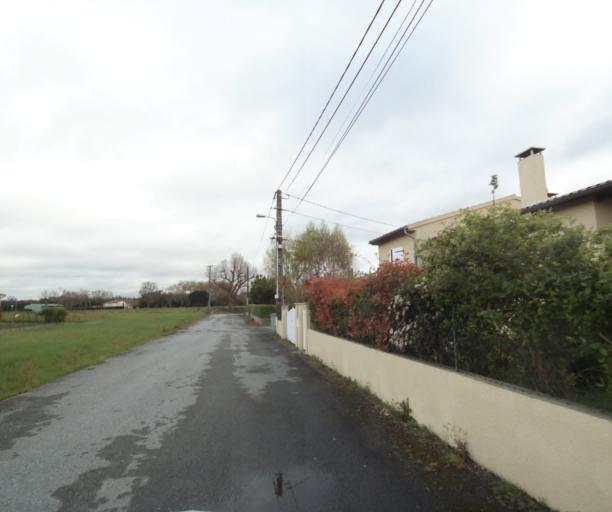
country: FR
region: Midi-Pyrenees
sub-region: Departement de l'Ariege
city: Saverdun
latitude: 43.2450
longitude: 1.5731
